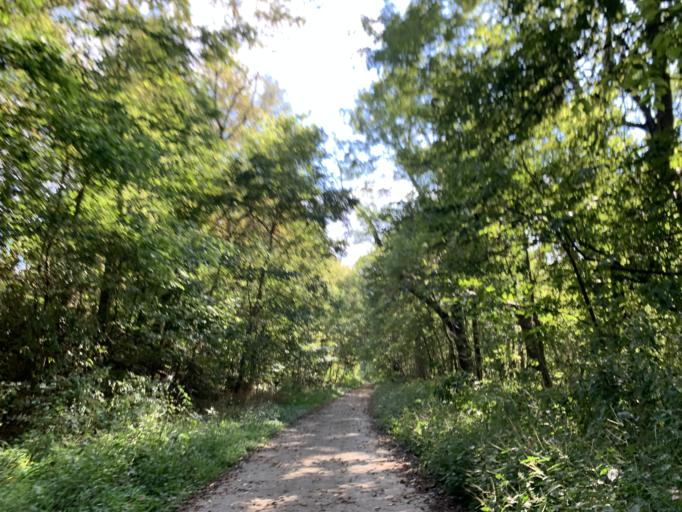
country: US
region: Indiana
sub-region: Floyd County
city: New Albany
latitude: 38.2536
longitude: -85.8325
